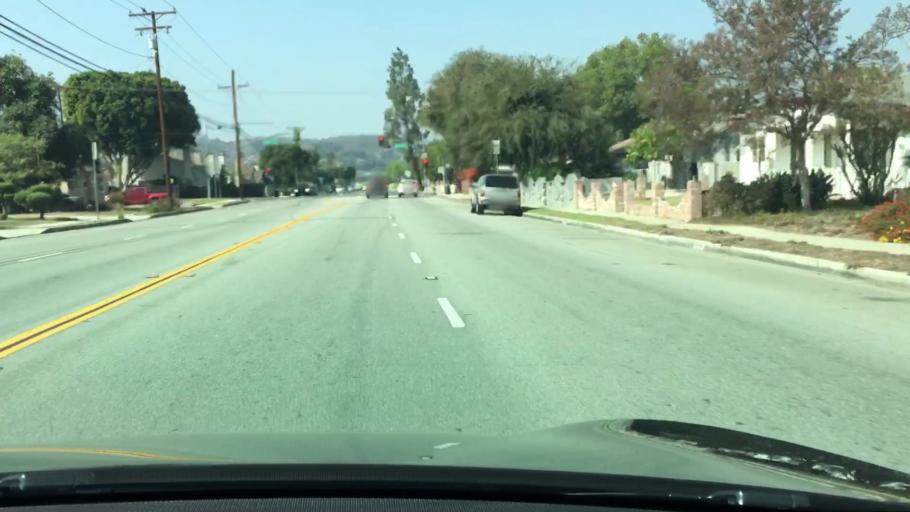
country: US
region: California
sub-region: Los Angeles County
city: Avocado Heights
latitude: 34.0163
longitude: -117.9789
